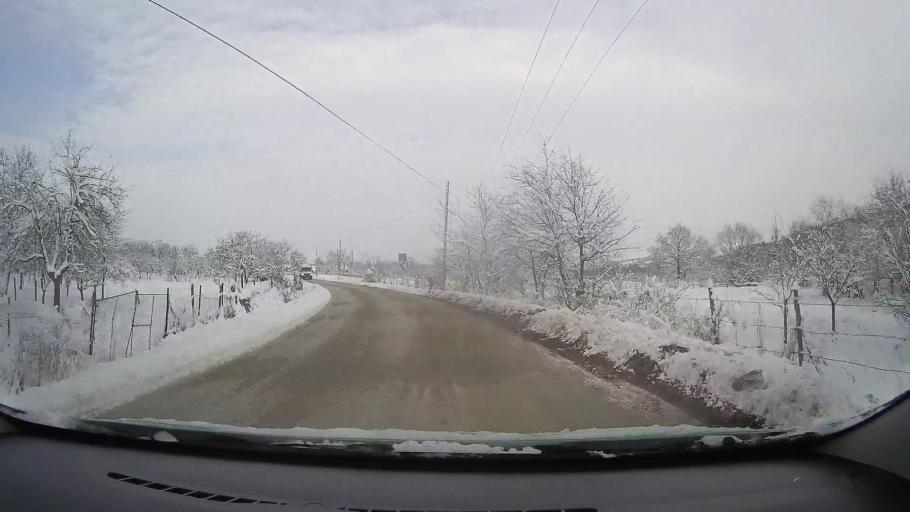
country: RO
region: Alba
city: Pianu de Sus
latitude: 45.9061
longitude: 23.4806
